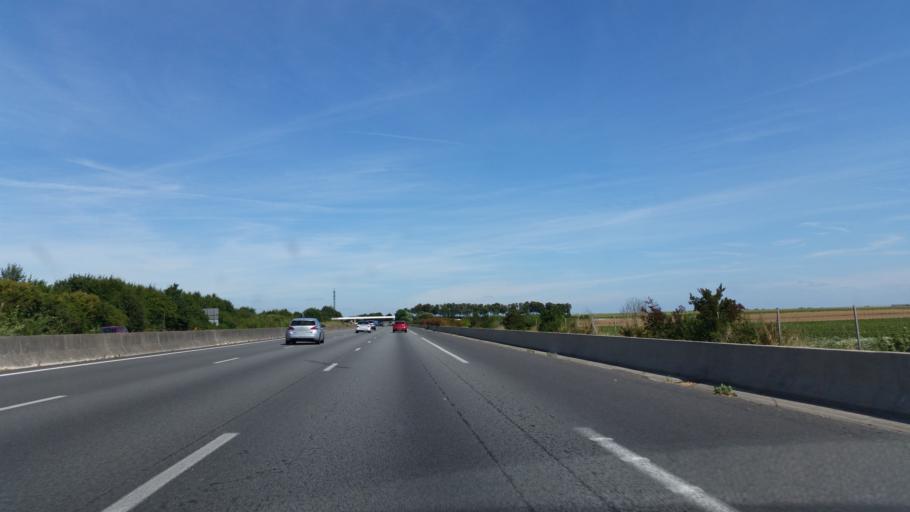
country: FR
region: Nord-Pas-de-Calais
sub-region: Departement du Pas-de-Calais
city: Vitry-en-Artois
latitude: 50.3513
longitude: 2.9481
